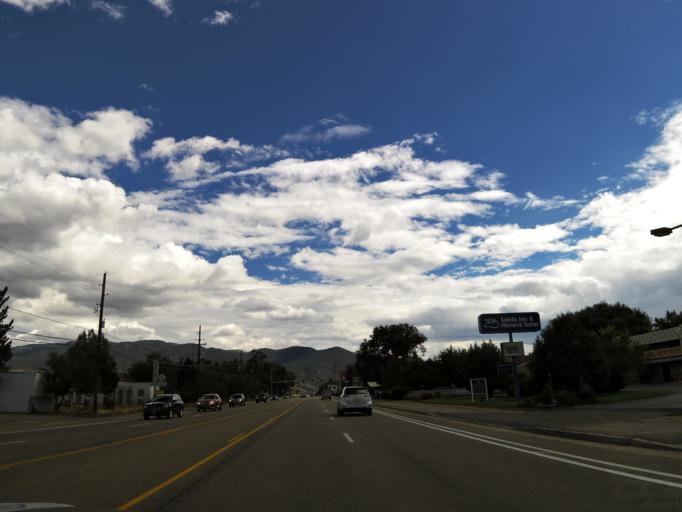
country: US
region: Colorado
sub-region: Chaffee County
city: Salida
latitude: 38.5242
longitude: -106.0132
